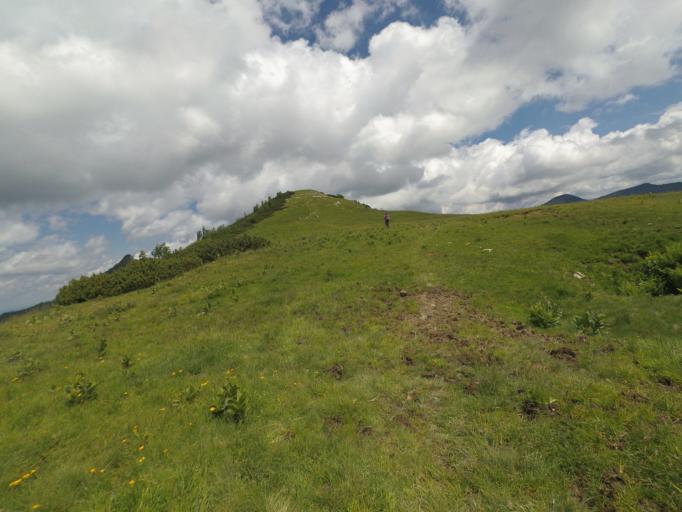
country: AT
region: Salzburg
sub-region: Politischer Bezirk Salzburg-Umgebung
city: Hintersee
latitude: 47.6643
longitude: 13.2972
